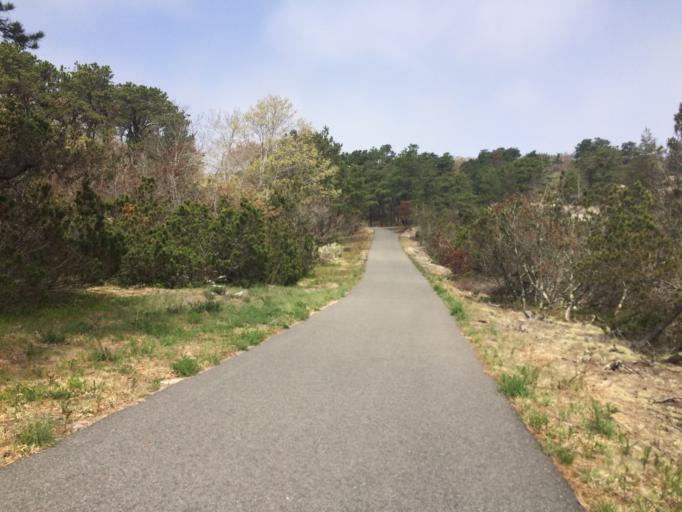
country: US
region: Massachusetts
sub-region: Barnstable County
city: Provincetown
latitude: 42.0690
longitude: -70.1945
